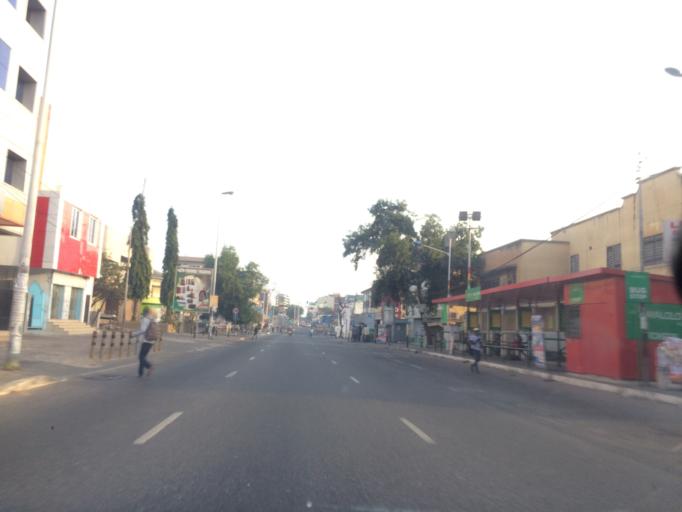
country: GH
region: Greater Accra
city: Accra
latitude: 5.5580
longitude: -0.2125
